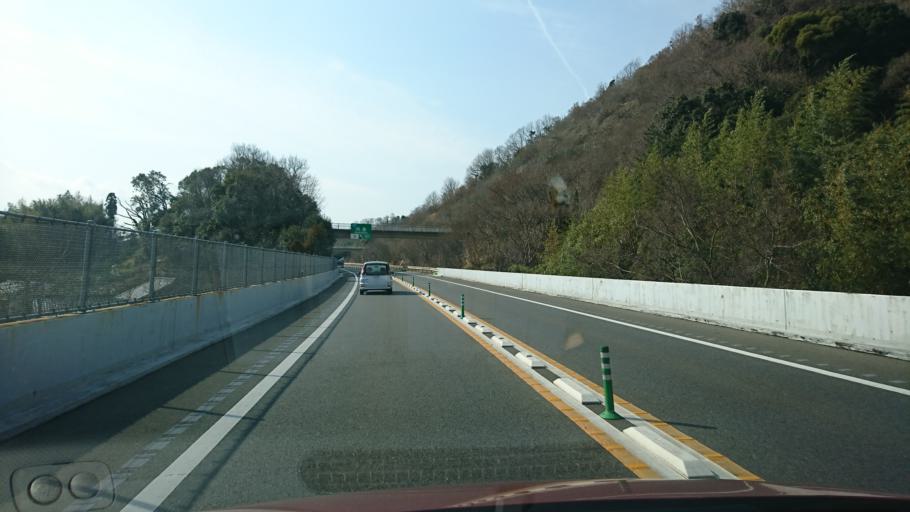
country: JP
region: Hiroshima
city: Onomichi
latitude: 34.3845
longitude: 133.1965
